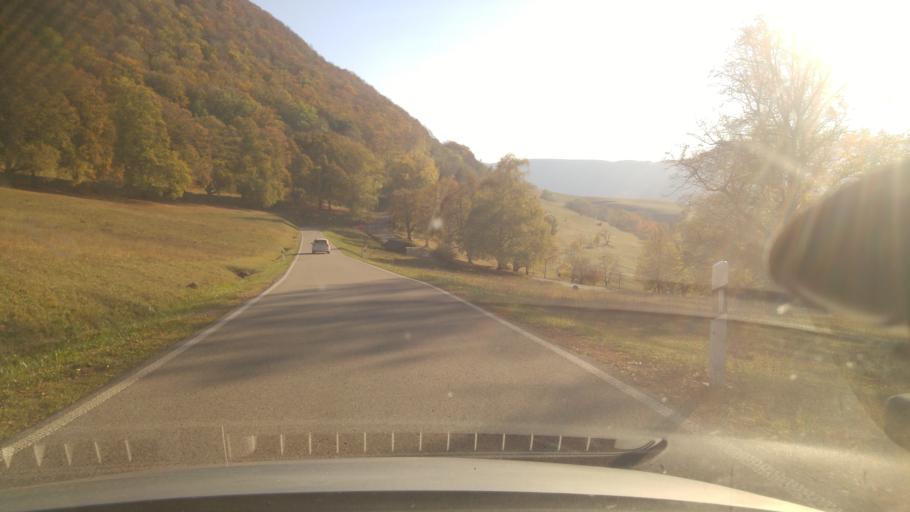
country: DE
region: Baden-Wuerttemberg
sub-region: Regierungsbezirk Stuttgart
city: Owen
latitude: 48.5934
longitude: 9.4675
